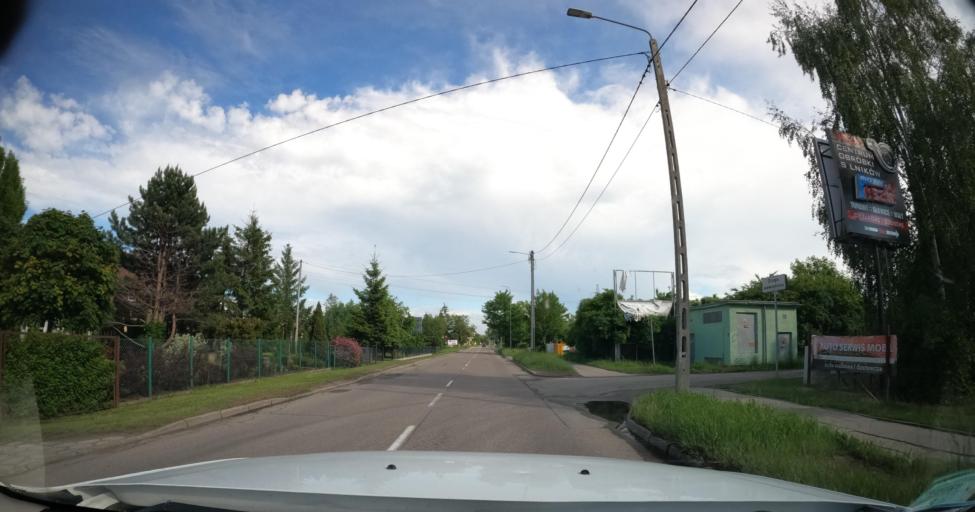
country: PL
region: Warmian-Masurian Voivodeship
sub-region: Powiat elblaski
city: Elblag
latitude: 54.1640
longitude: 19.3792
